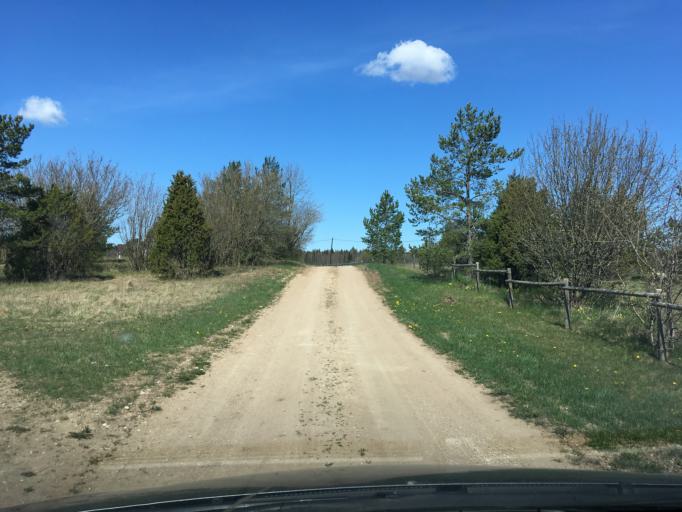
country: EE
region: Harju
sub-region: Raasiku vald
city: Raasiku
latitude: 59.2214
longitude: 25.1525
